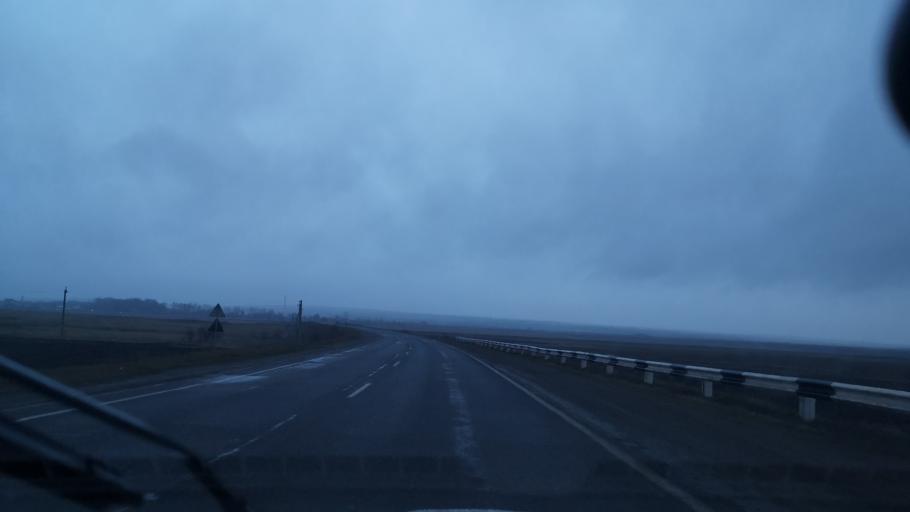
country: MD
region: Balti
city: Balti
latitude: 47.7531
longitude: 27.9634
